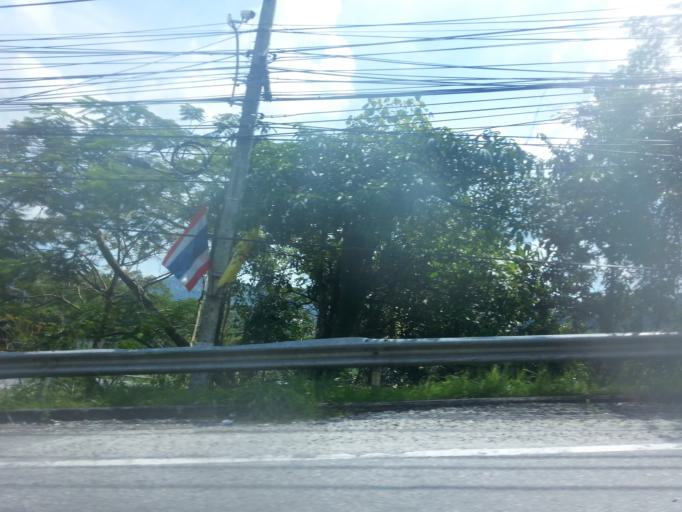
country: TH
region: Phuket
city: Kathu
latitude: 7.9056
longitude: 98.3237
